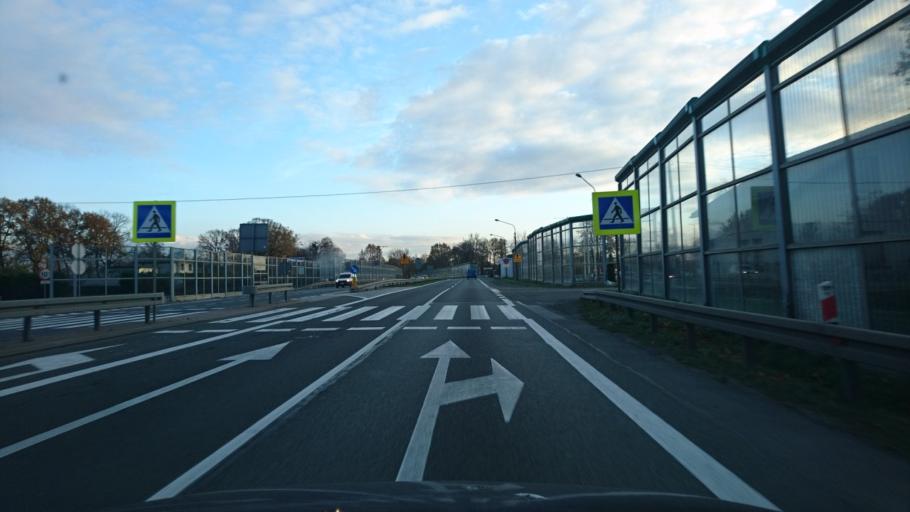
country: PL
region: Silesian Voivodeship
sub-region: Powiat pszczynski
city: Goczalkowice Zdroj
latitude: 49.9383
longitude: 18.9838
